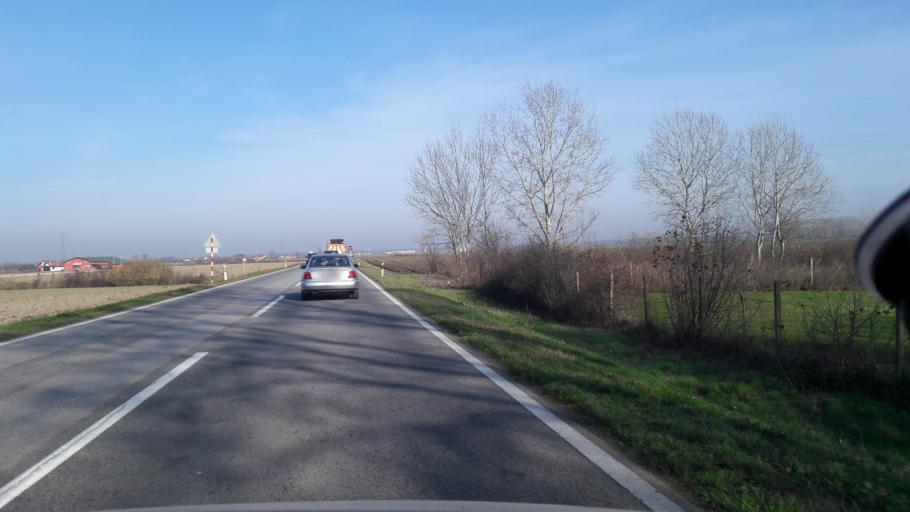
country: HR
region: Vukovarsko-Srijemska
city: Gradiste
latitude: 45.1336
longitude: 18.7195
